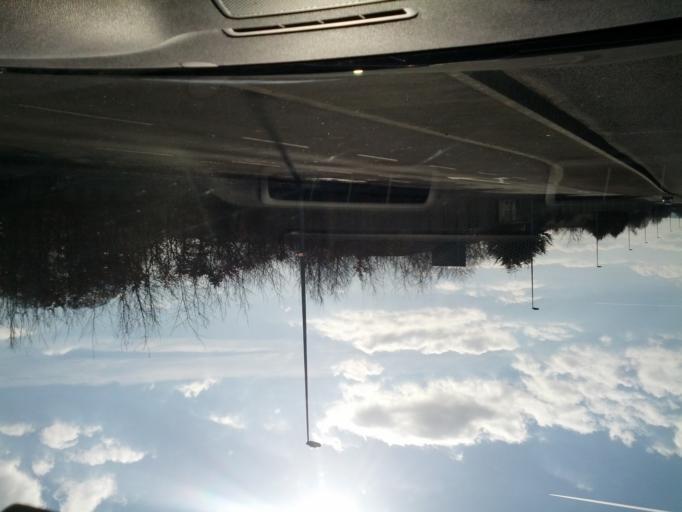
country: IE
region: Leinster
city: Lucan
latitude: 53.3468
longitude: -6.4250
